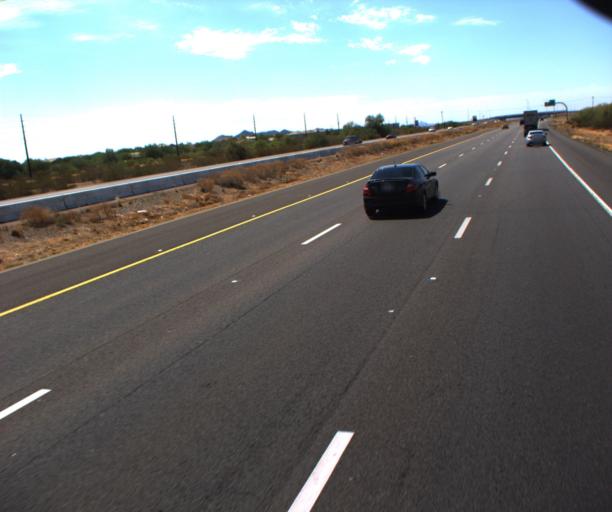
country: US
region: Arizona
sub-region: Maricopa County
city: Anthem
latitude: 33.8085
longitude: -112.1379
